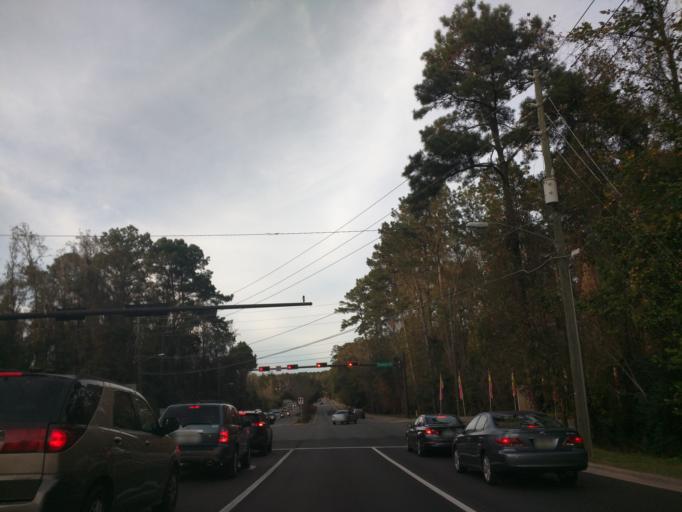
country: US
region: Florida
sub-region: Leon County
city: Tallahassee
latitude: 30.4374
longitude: -84.2495
